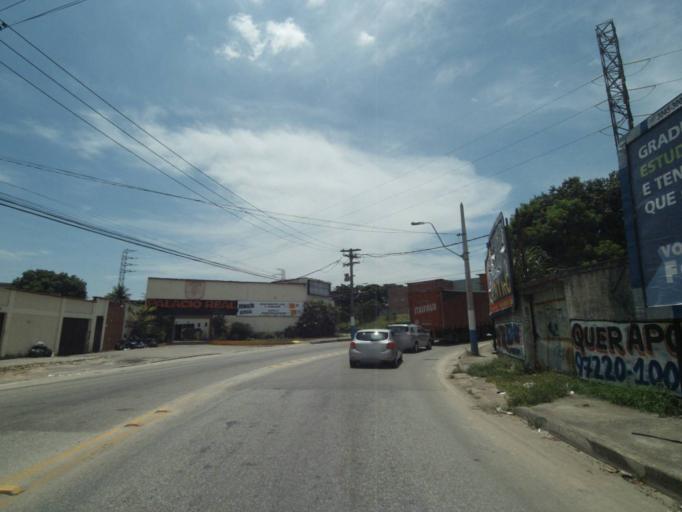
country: BR
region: Rio de Janeiro
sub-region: Sao Joao De Meriti
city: Sao Joao de Meriti
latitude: -22.7996
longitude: -43.3559
